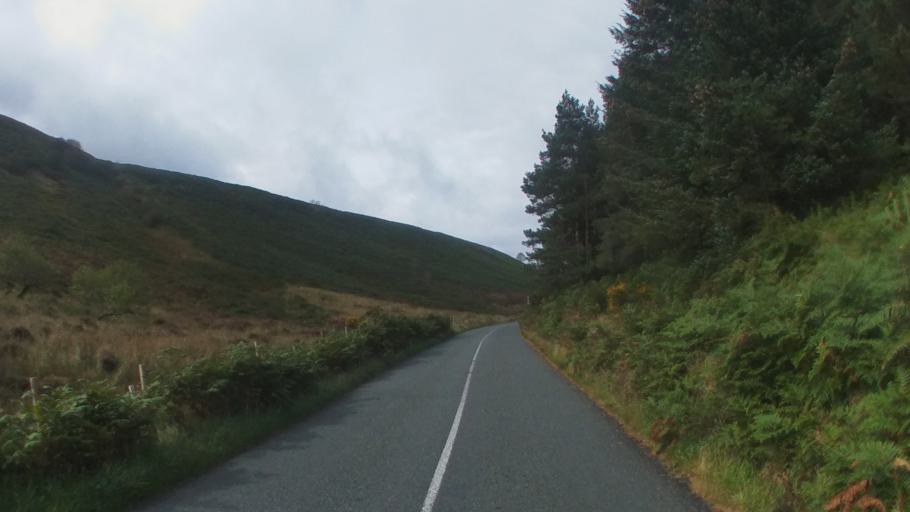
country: IE
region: Leinster
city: Ballinteer
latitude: 53.2334
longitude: -6.2782
